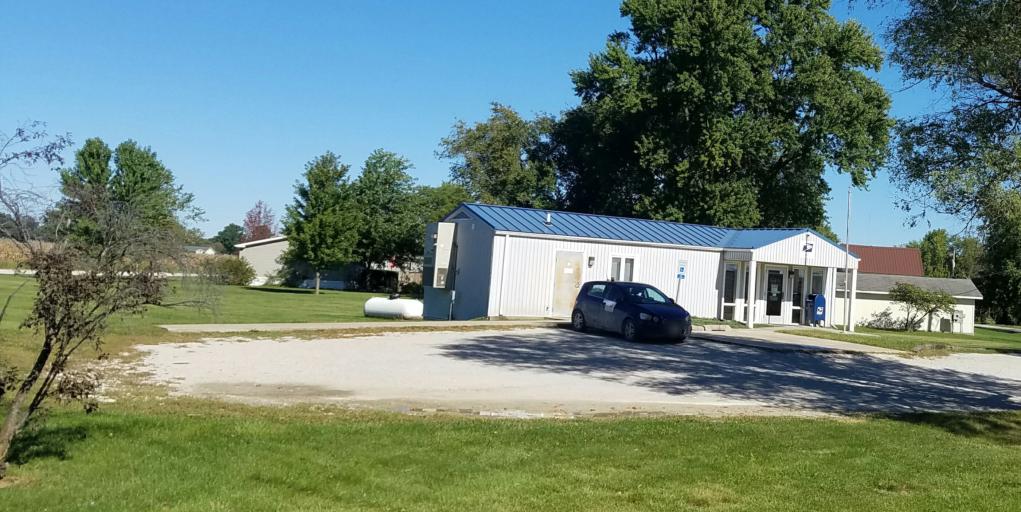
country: US
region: Iowa
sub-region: Decatur County
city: Lamoni
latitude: 40.6343
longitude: -93.8146
